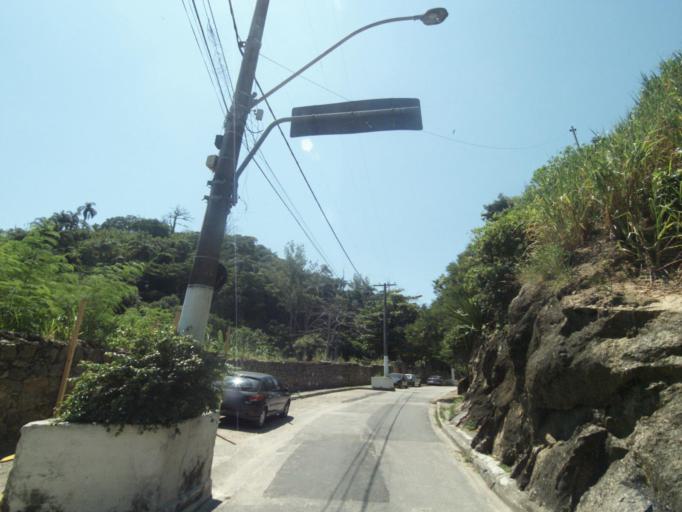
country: BR
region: Rio de Janeiro
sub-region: Niteroi
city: Niteroi
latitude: -22.9278
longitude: -43.1222
